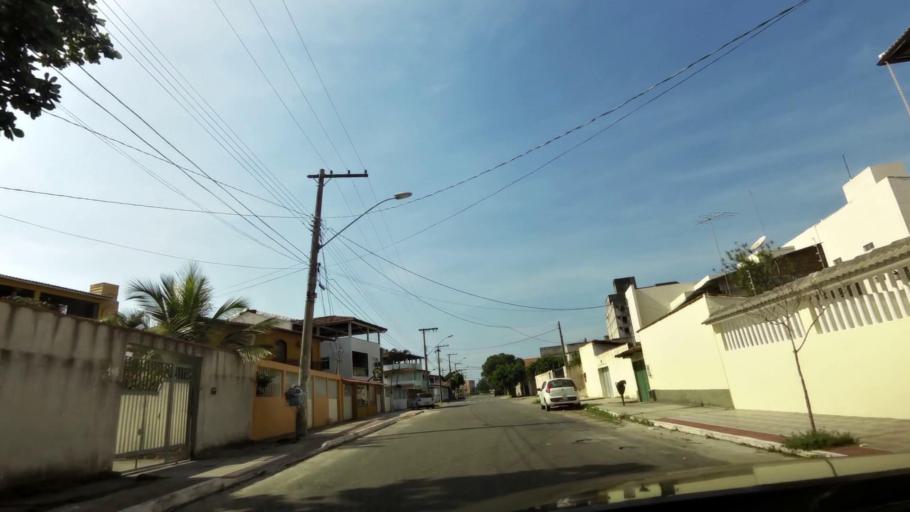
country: BR
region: Espirito Santo
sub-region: Guarapari
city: Guarapari
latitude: -20.6548
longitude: -40.4947
